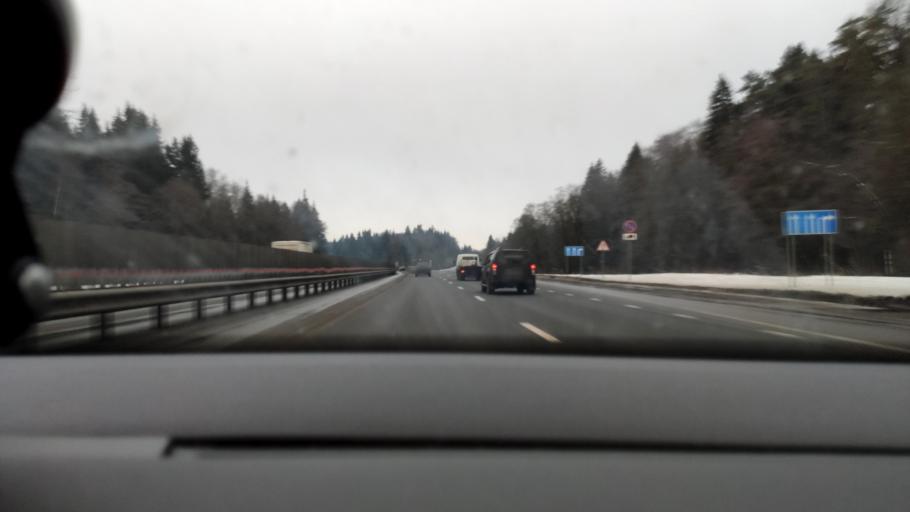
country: RU
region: Moskovskaya
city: Ashukino
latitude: 56.1780
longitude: 38.0229
